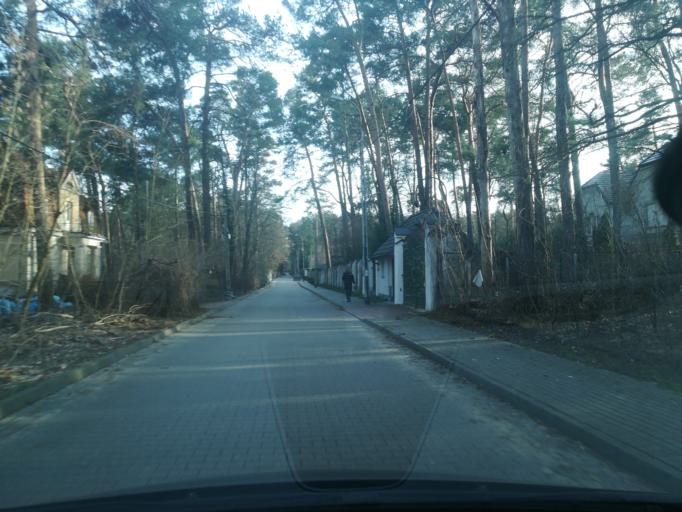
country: PL
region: Masovian Voivodeship
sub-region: Powiat piaseczynski
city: Konstancin-Jeziorna
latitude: 52.0795
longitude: 21.1070
